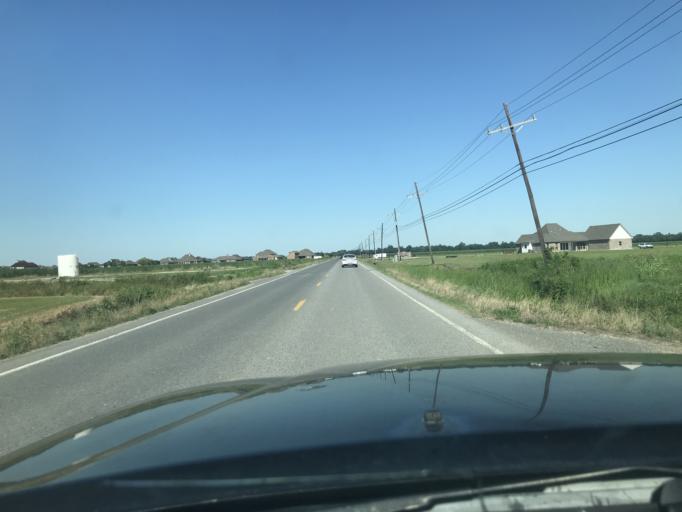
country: US
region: Louisiana
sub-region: West Baton Rouge Parish
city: Brusly
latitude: 30.4685
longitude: -91.3089
